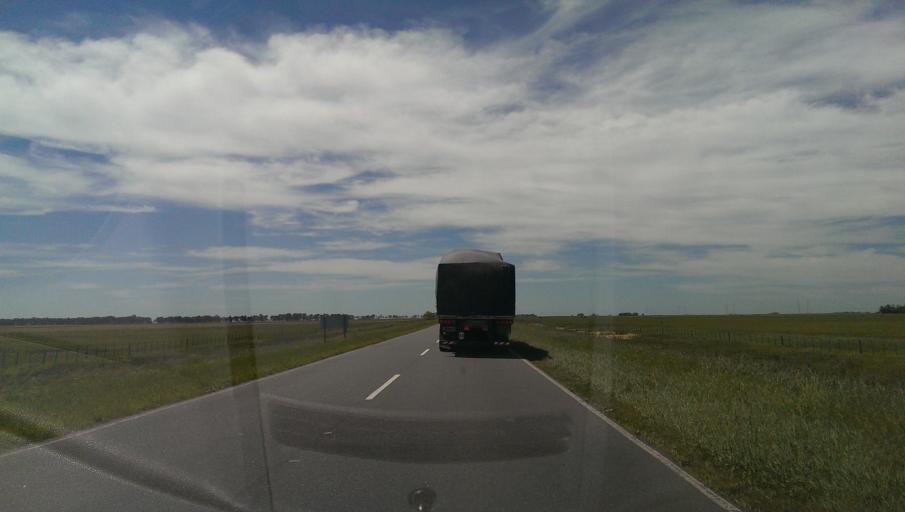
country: AR
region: Buenos Aires
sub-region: Partido de Laprida
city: Laprida
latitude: -37.2967
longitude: -60.8735
